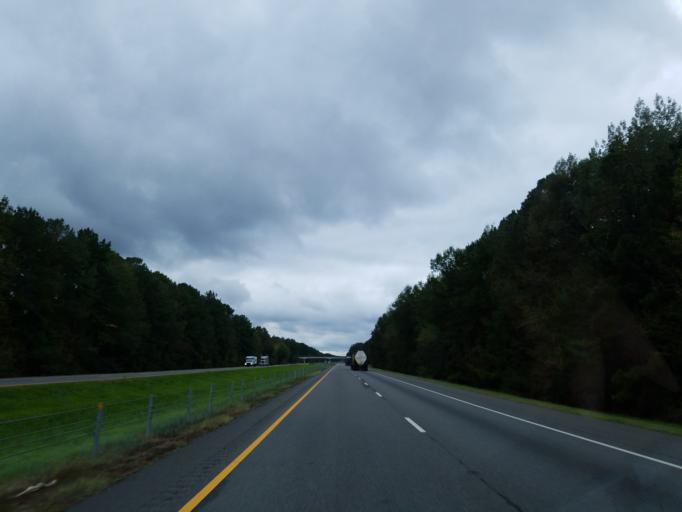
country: US
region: Alabama
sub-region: Greene County
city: Eutaw
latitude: 32.7642
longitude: -88.0678
